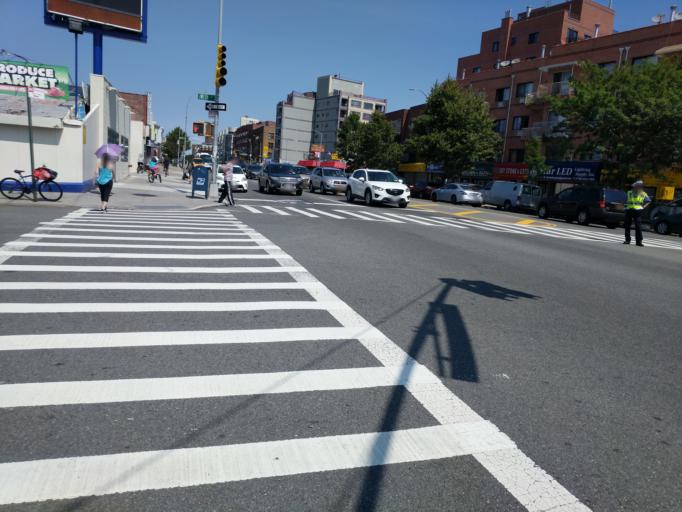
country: US
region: New York
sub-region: Queens County
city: Jamaica
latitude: 40.7523
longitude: -73.8326
